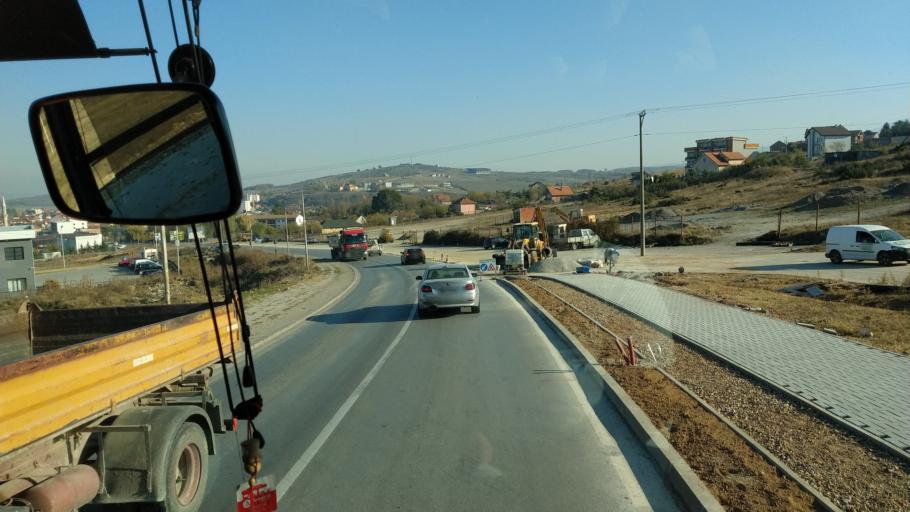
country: XK
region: Ferizaj
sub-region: Komuna e Shtimes
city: Shtime
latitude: 42.4364
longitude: 21.0240
